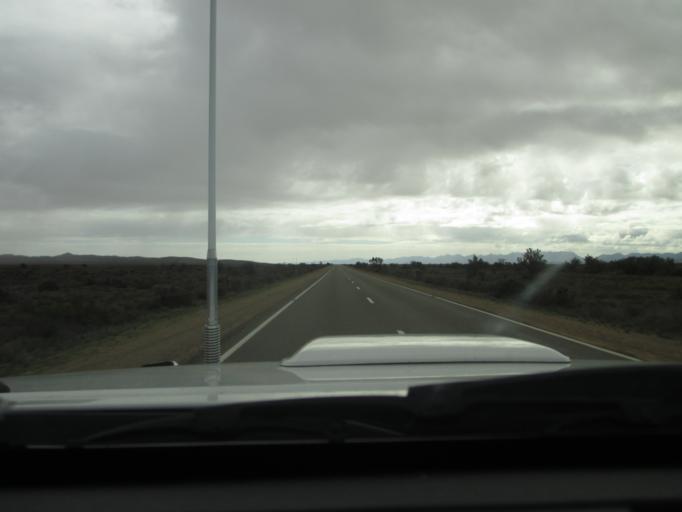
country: AU
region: South Australia
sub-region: Flinders Ranges
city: Quorn
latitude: -31.5372
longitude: 138.4252
